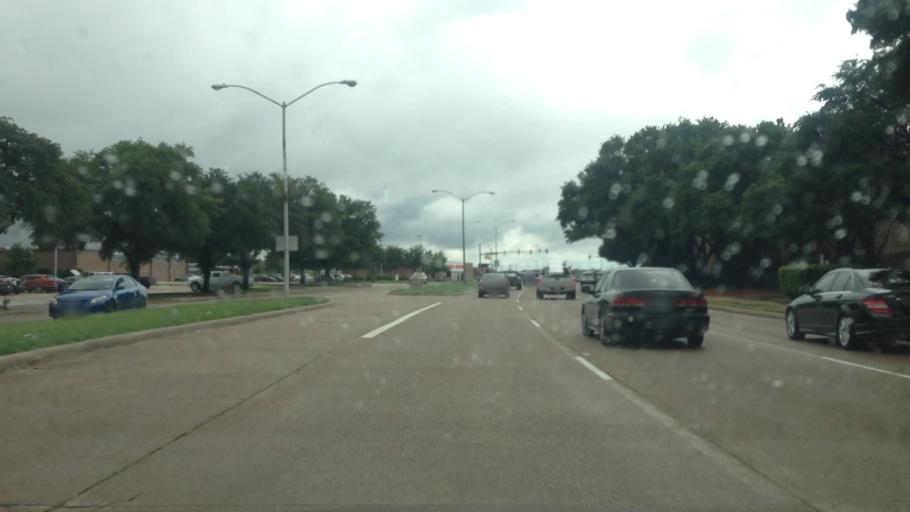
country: US
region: Texas
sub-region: Tarrant County
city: Edgecliff Village
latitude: 32.6687
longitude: -97.4001
